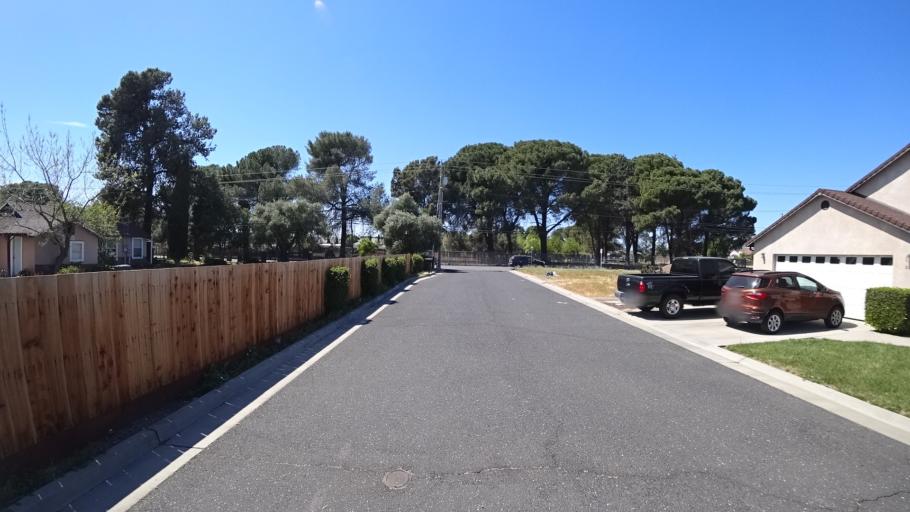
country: US
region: California
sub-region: Glenn County
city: Orland
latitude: 39.7430
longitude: -122.1775
